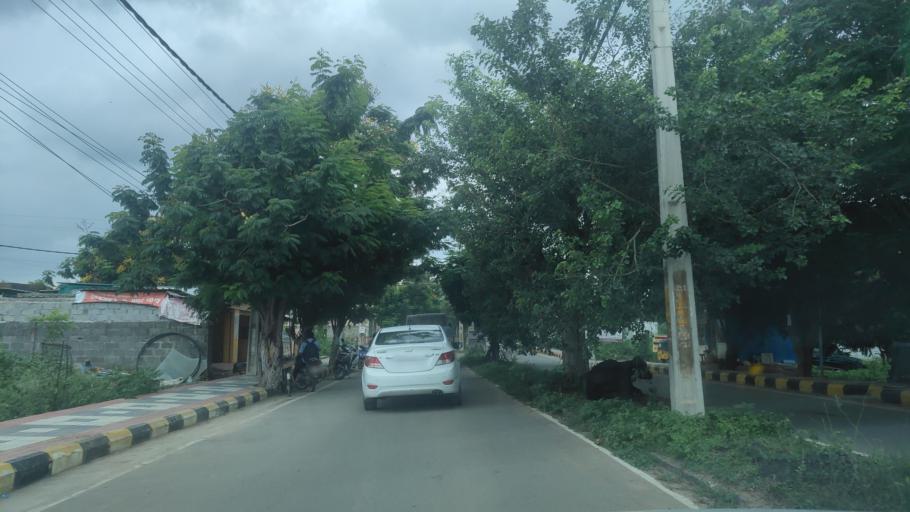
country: IN
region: Telangana
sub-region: Medak
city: Serilingampalle
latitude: 17.5025
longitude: 78.3516
